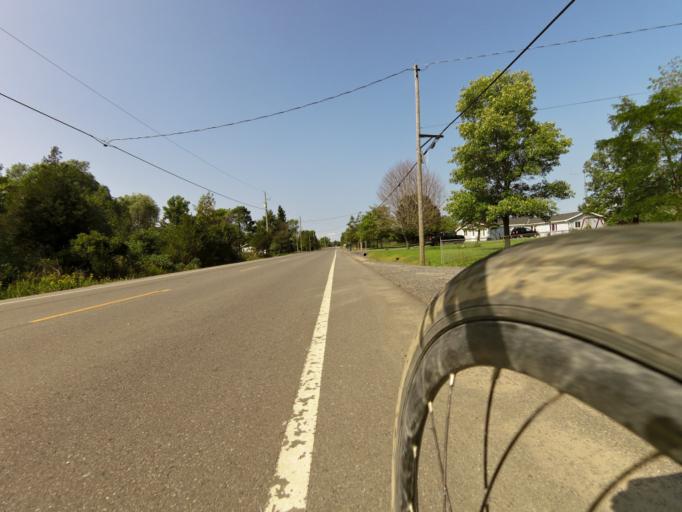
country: CA
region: Ontario
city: Skatepark
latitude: 44.2575
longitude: -76.7239
